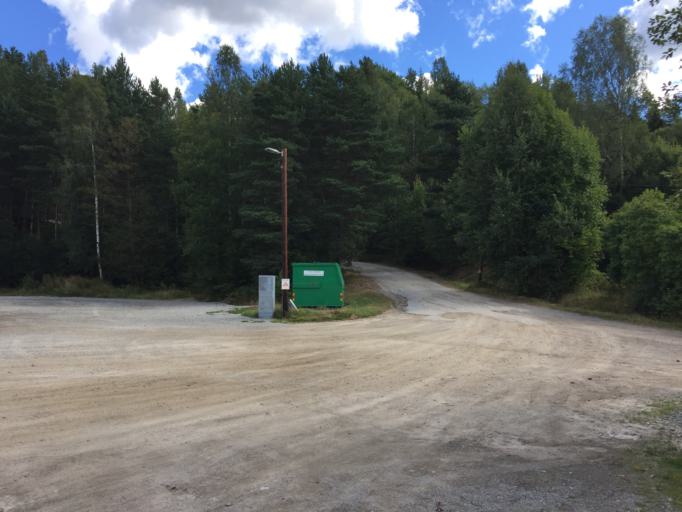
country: SE
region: Stockholm
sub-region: Botkyrka Kommun
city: Varsta
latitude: 59.1739
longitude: 17.7933
